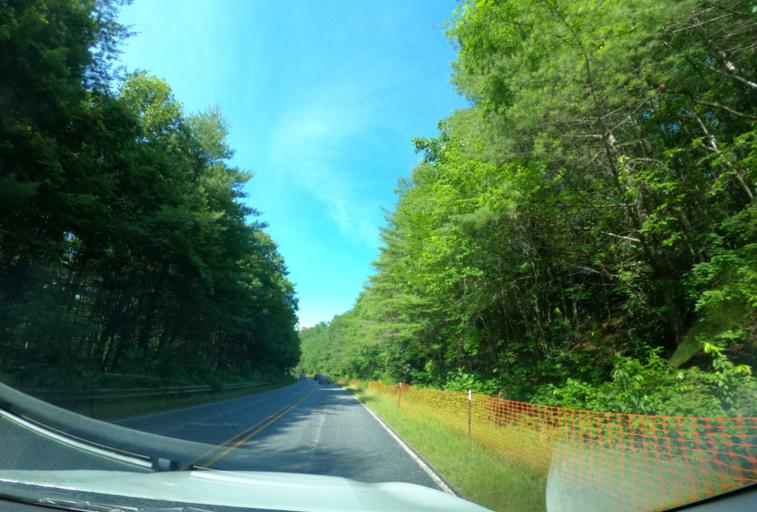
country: US
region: North Carolina
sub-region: Transylvania County
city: Brevard
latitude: 35.1993
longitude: -82.6207
